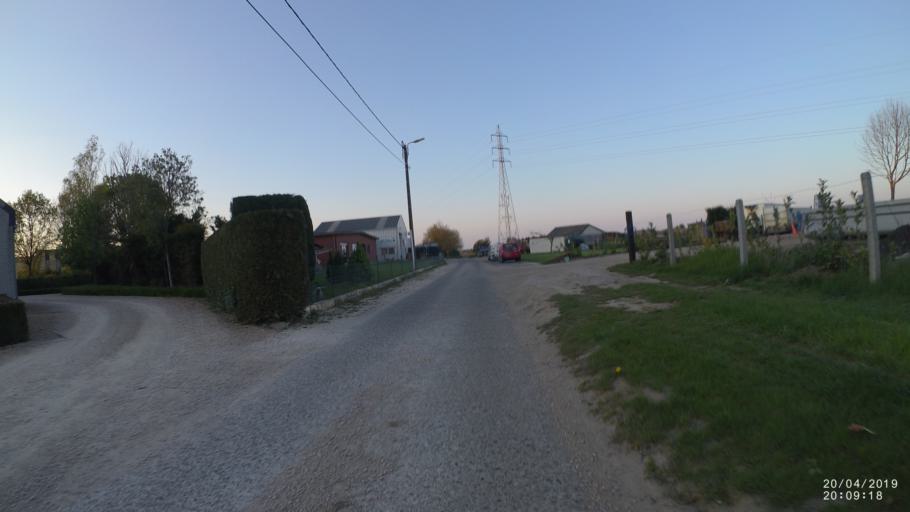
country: BE
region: Flanders
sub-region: Provincie Vlaams-Brabant
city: Lubbeek
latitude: 50.8937
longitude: 4.8003
